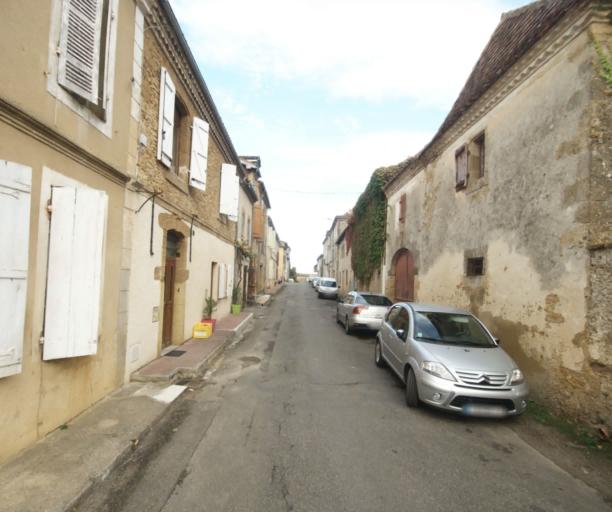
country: FR
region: Midi-Pyrenees
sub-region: Departement du Gers
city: Cazaubon
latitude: 43.8655
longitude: -0.1093
